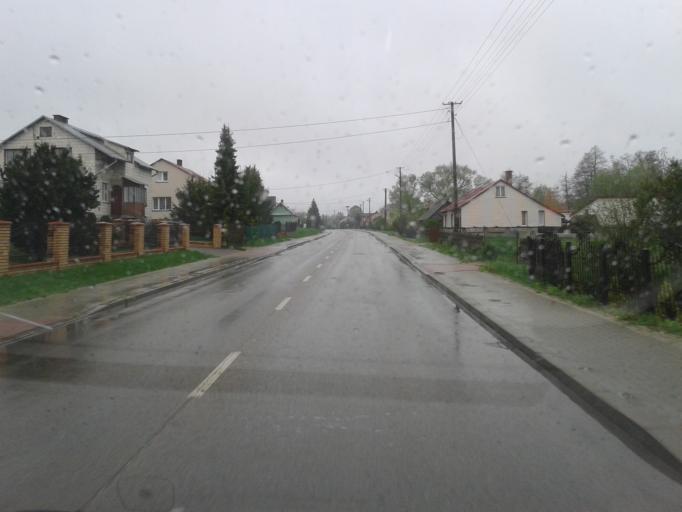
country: PL
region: Lublin Voivodeship
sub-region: Powiat tomaszowski
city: Belzec
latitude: 50.3827
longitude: 23.4136
